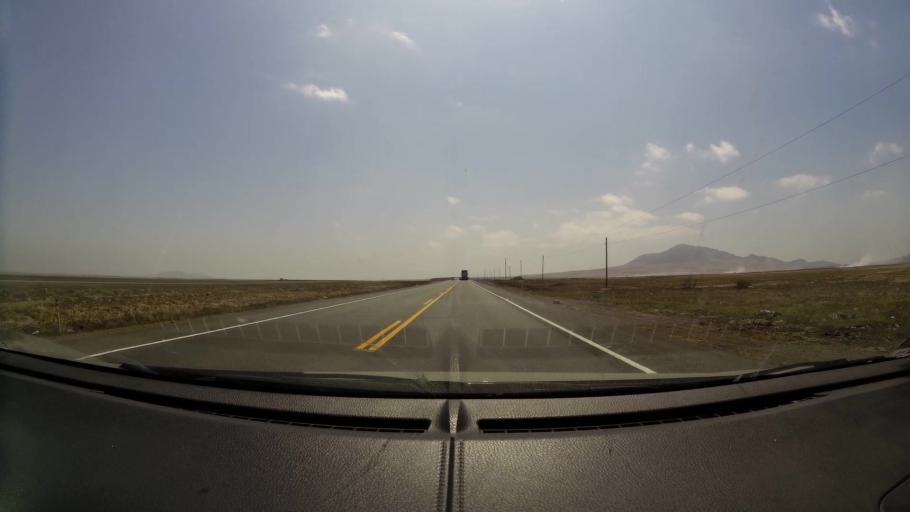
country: PE
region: Lambayeque
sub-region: Provincia de Chiclayo
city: Reque
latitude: -6.9330
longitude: -79.7328
